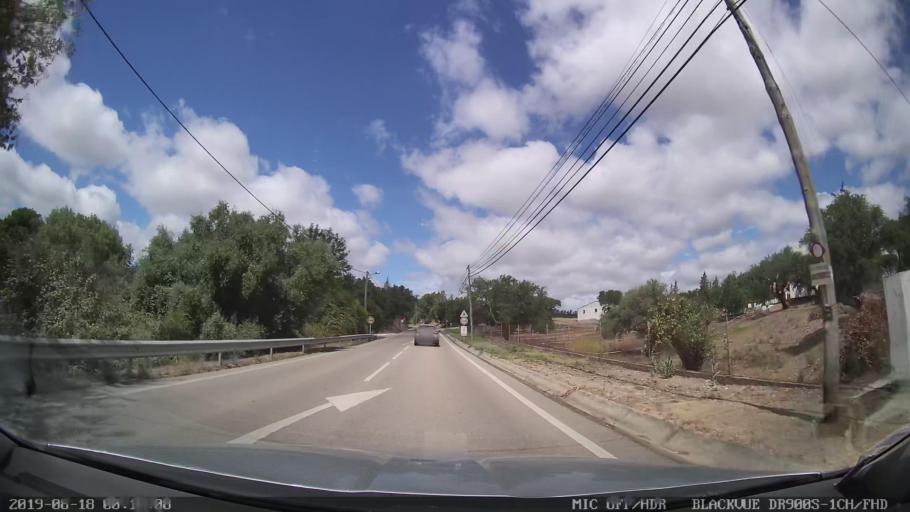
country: PT
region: Santarem
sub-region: Benavente
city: Poceirao
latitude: 38.8566
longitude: -8.7323
